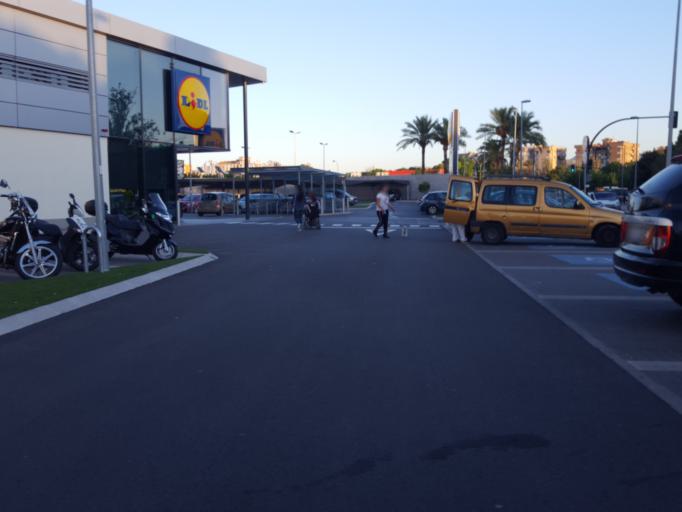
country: ES
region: Murcia
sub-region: Murcia
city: Murcia
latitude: 38.0022
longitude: -1.1451
